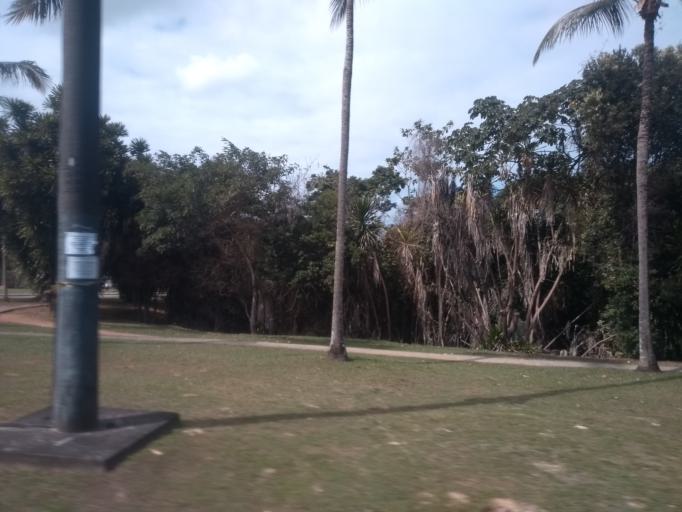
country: BR
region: Bahia
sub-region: Salvador
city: Salvador
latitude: -12.9446
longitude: -38.4241
